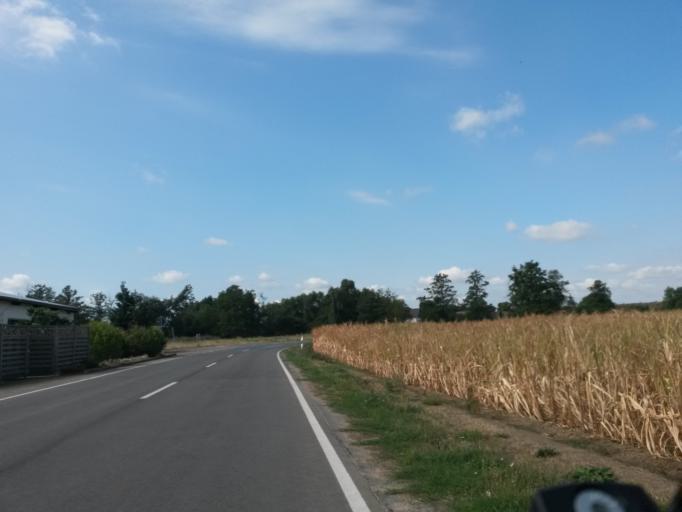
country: DE
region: Saxony-Anhalt
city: Elster
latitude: 51.8125
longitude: 12.7901
